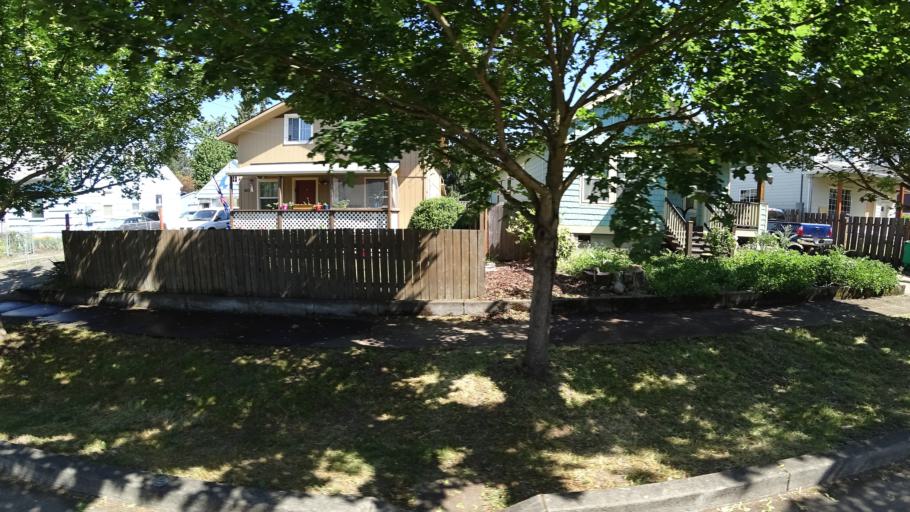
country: US
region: Oregon
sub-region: Multnomah County
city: Lents
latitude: 45.4818
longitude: -122.5549
